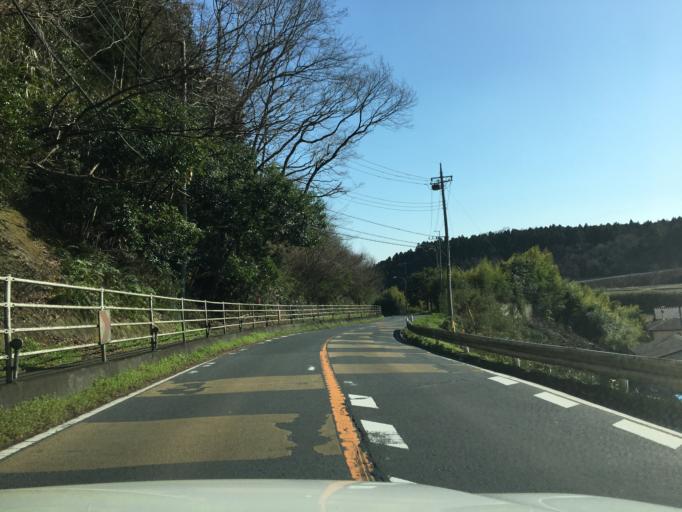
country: JP
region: Ibaraki
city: Omiya
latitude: 36.4544
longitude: 140.4077
